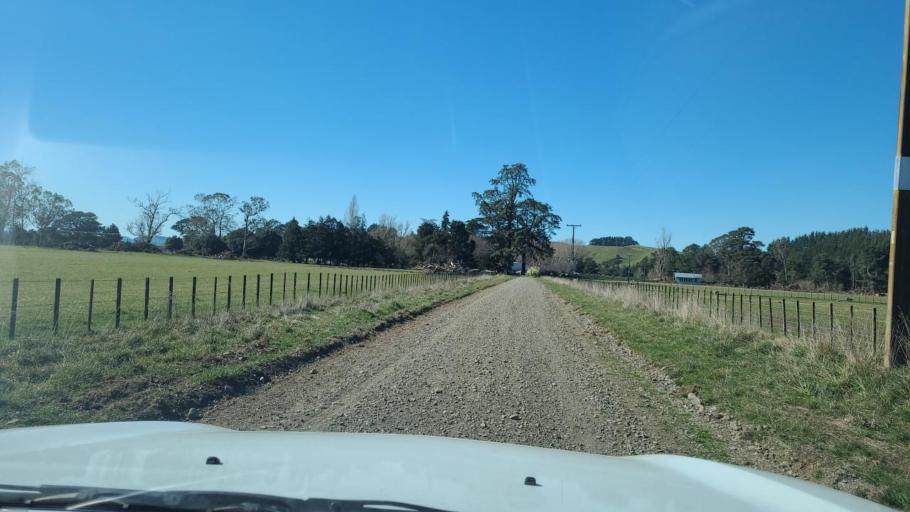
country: NZ
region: Hawke's Bay
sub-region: Napier City
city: Taradale
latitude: -39.4645
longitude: 176.6003
